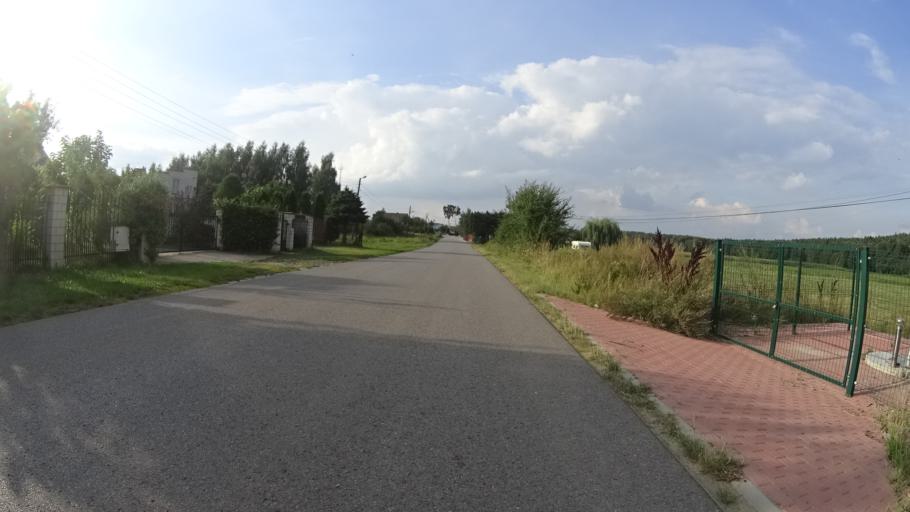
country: PL
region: Masovian Voivodeship
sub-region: Powiat grojecki
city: Mogielnica
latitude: 51.6825
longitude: 20.7319
